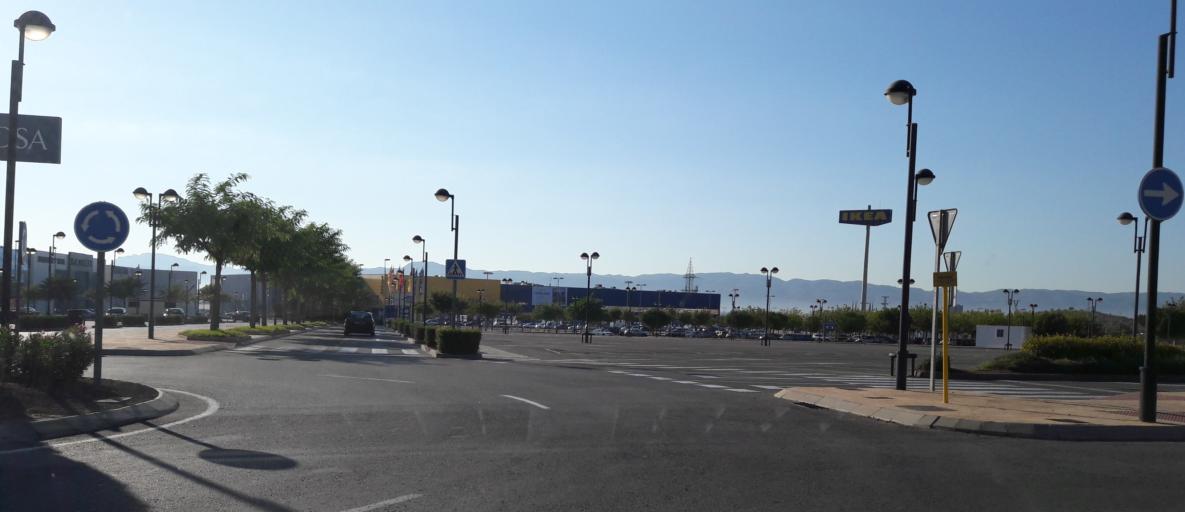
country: ES
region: Murcia
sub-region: Murcia
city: Murcia
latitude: 38.0305
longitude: -1.1476
